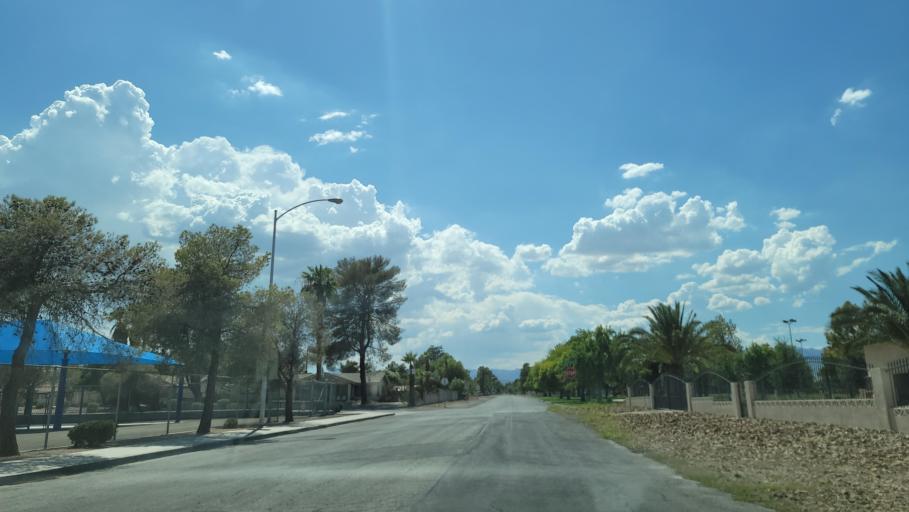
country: US
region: Nevada
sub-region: Clark County
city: Spring Valley
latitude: 36.1386
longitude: -115.2354
